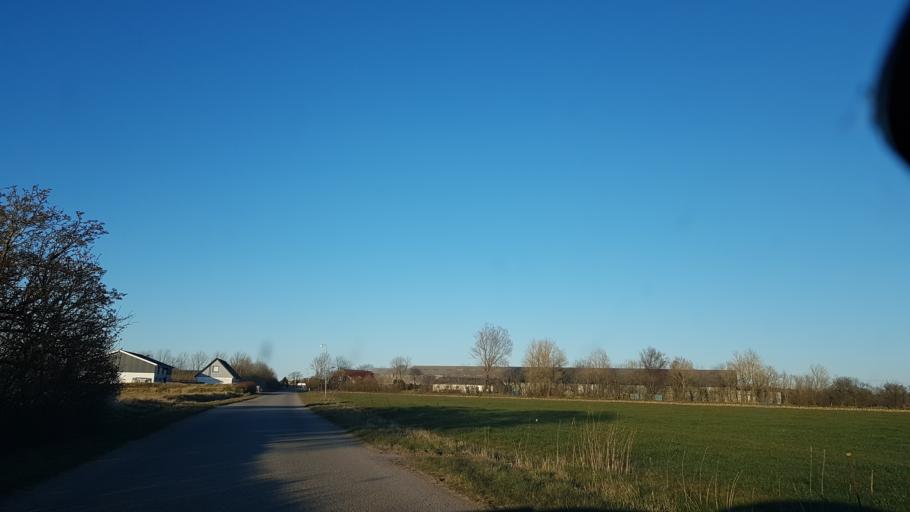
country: DK
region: South Denmark
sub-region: Esbjerg Kommune
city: Ribe
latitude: 55.3896
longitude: 8.7154
